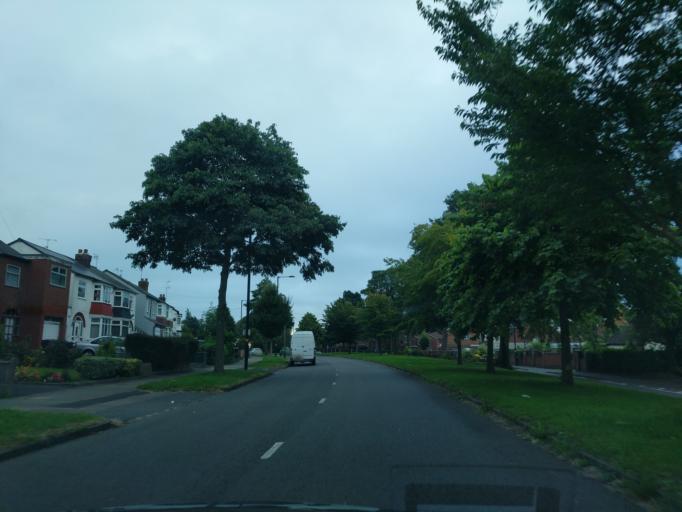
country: GB
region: England
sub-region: City and Borough of Birmingham
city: Bartley Green
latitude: 52.4593
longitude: -2.0065
